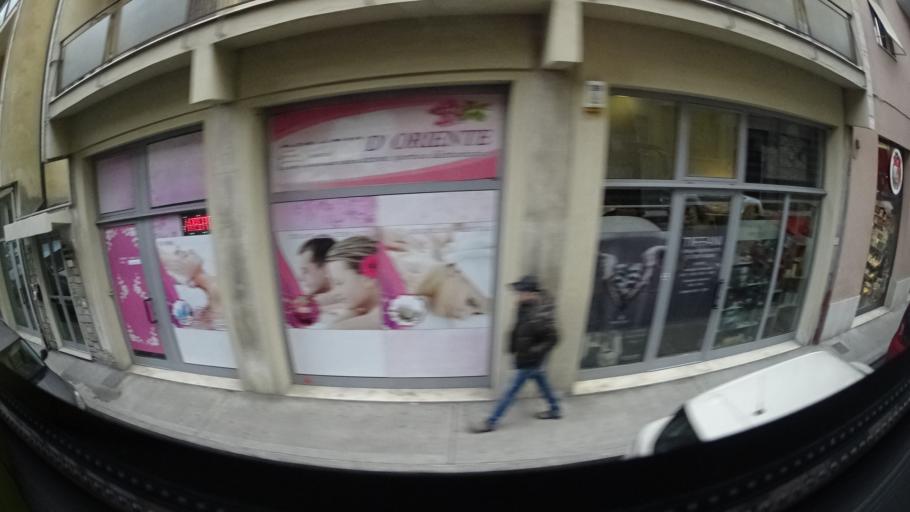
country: IT
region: Tuscany
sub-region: Provincia di Siena
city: Poggibonsi
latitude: 43.4668
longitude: 11.1491
